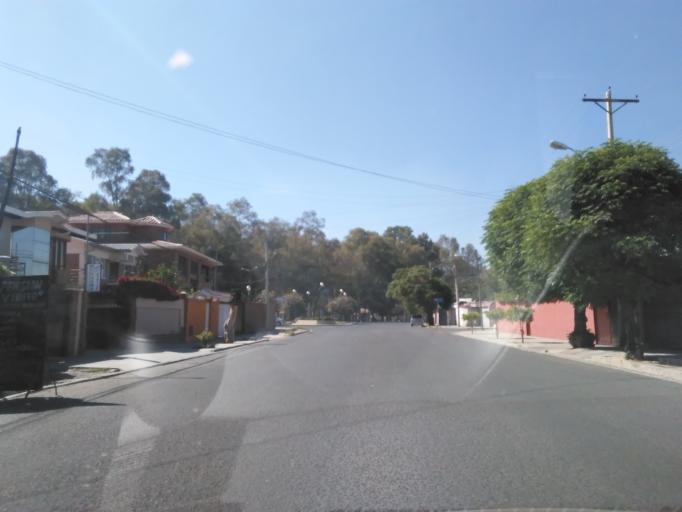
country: BO
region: Cochabamba
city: Cochabamba
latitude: -17.4006
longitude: -66.1769
